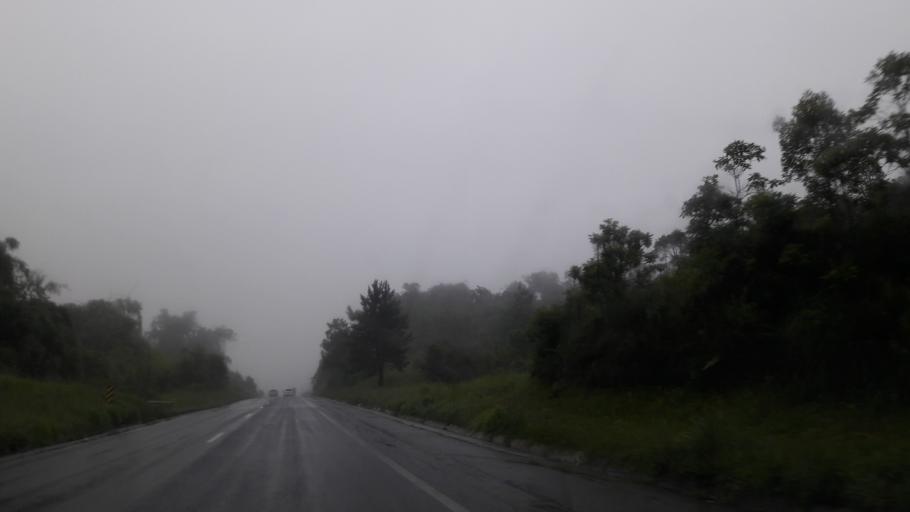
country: BR
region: Parana
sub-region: Antonina
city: Antonina
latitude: -25.1090
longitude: -48.7633
